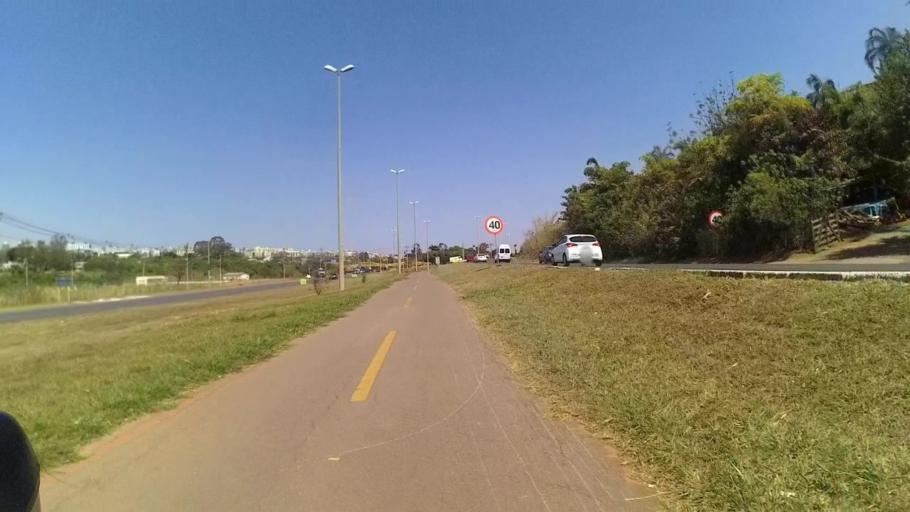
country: BR
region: Federal District
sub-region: Brasilia
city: Brasilia
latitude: -15.7159
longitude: -47.8699
